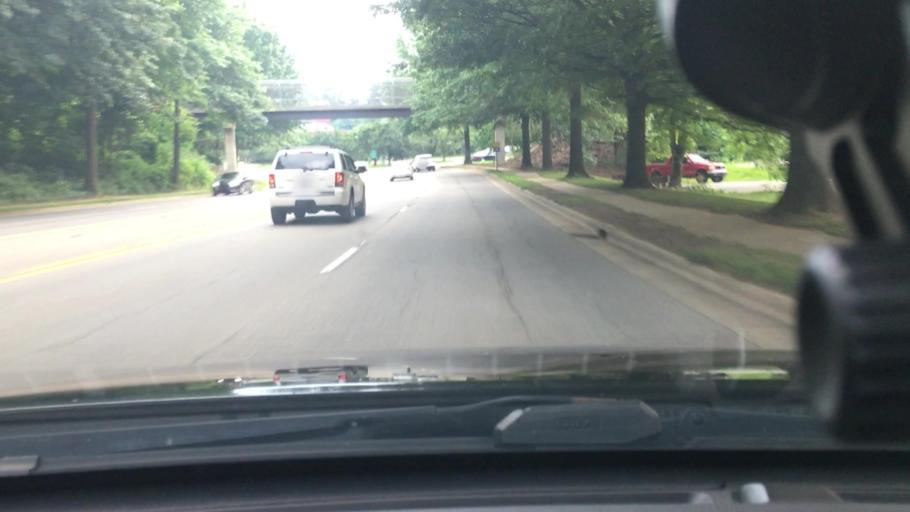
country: US
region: North Carolina
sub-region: Buncombe County
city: Asheville
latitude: 35.5950
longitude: -82.5470
